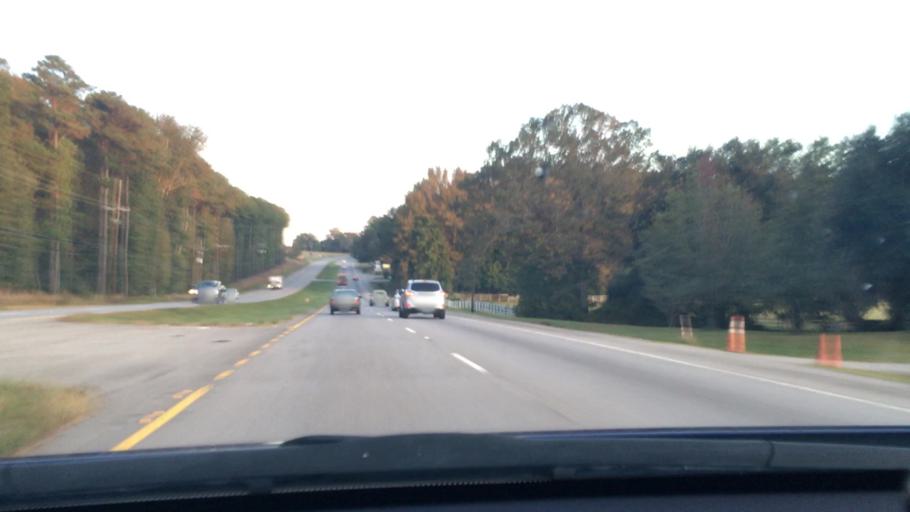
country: US
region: South Carolina
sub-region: Richland County
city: Hopkins
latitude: 33.9490
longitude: -80.8166
